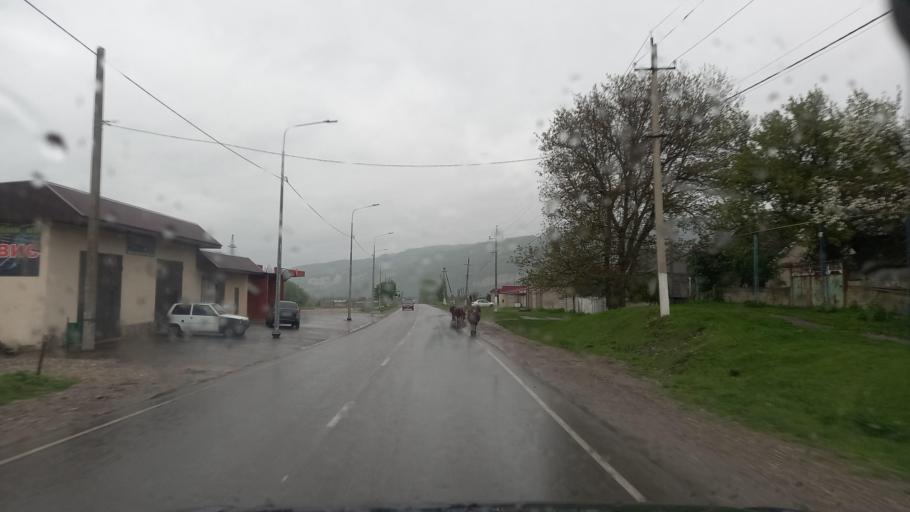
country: RU
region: Kabardino-Balkariya
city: Zhankhoteko
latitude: 43.5883
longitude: 43.2162
